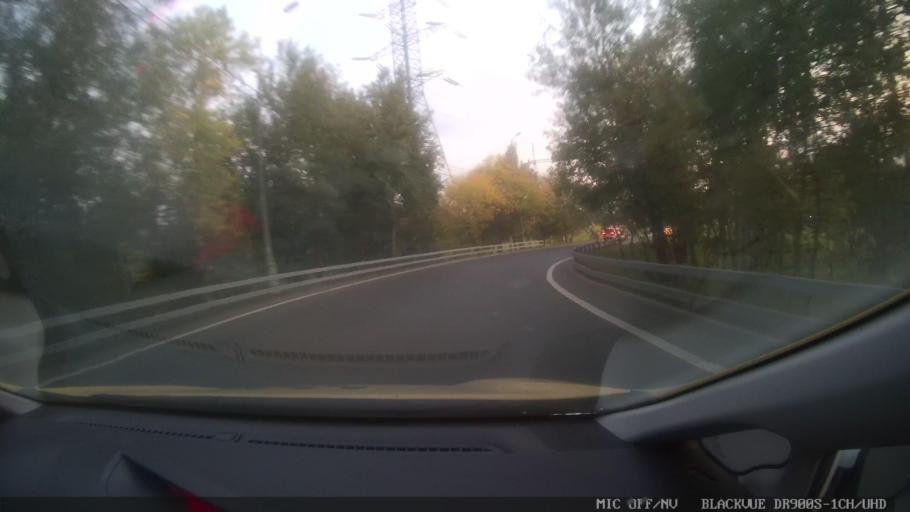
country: RU
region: Moskovskaya
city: Kuskovo
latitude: 55.7434
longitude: 37.8441
